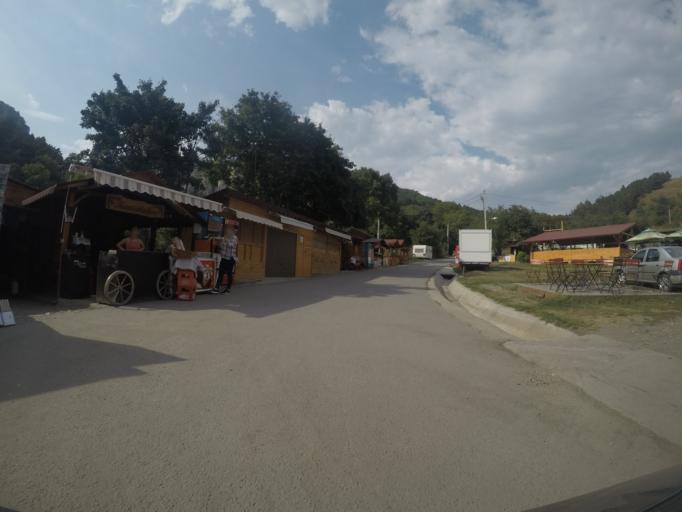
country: RO
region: Cluj
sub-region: Comuna Sandulesti
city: Sandulesti
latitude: 46.5615
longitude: 23.6912
